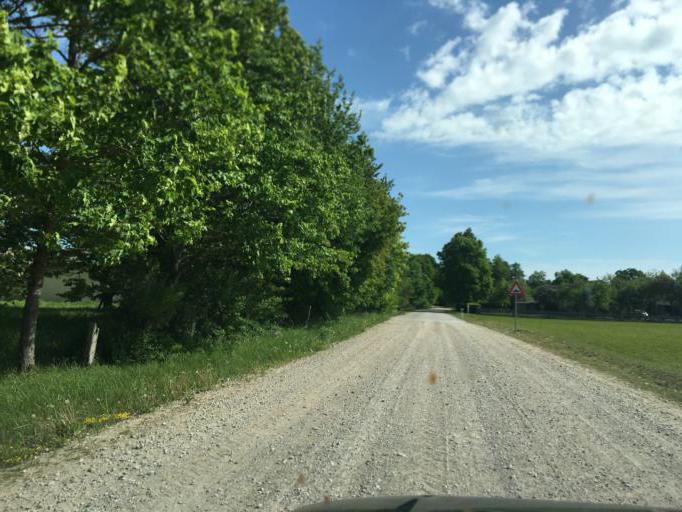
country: LV
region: Talsu Rajons
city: Valdemarpils
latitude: 57.3423
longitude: 22.4895
